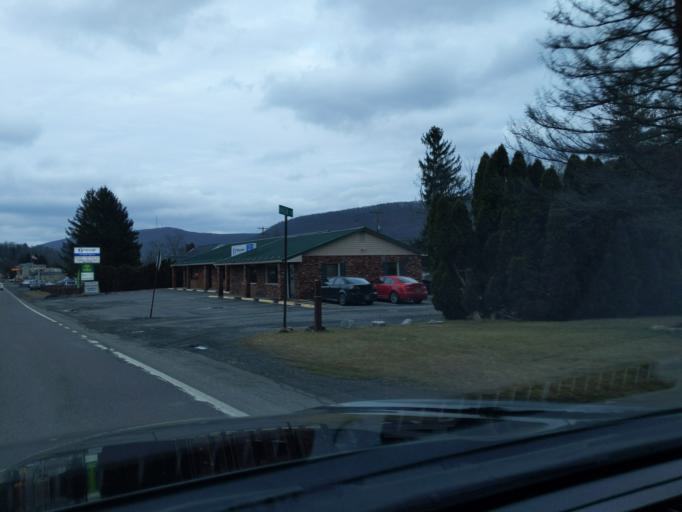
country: US
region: Pennsylvania
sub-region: Blair County
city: Tyrone
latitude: 40.6601
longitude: -78.2583
